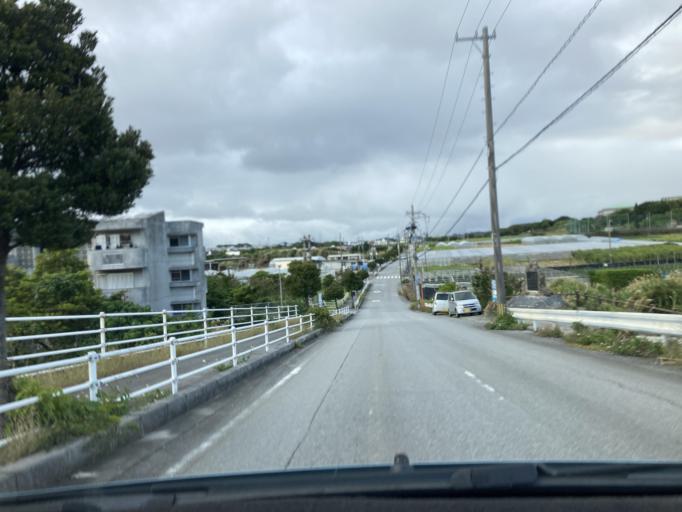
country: JP
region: Okinawa
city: Itoman
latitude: 26.1237
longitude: 127.6867
